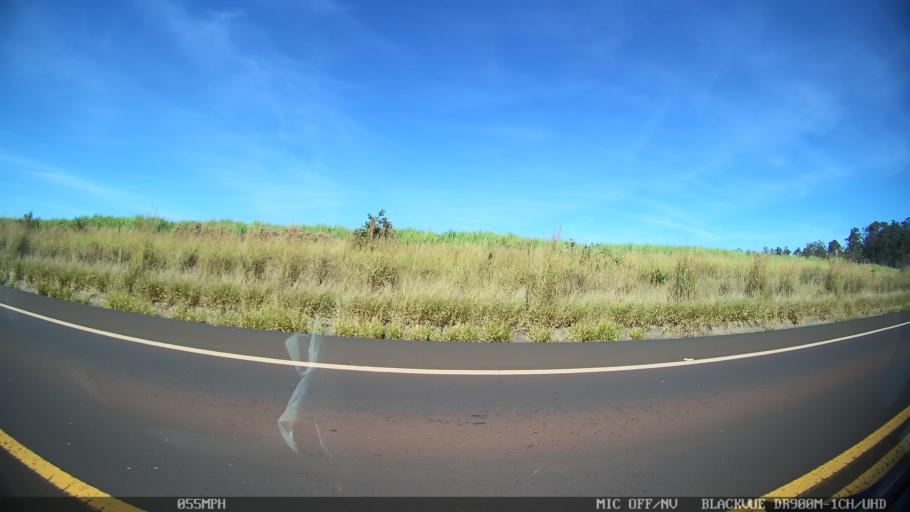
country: BR
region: Sao Paulo
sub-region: Franca
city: Franca
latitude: -20.5614
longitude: -47.5078
